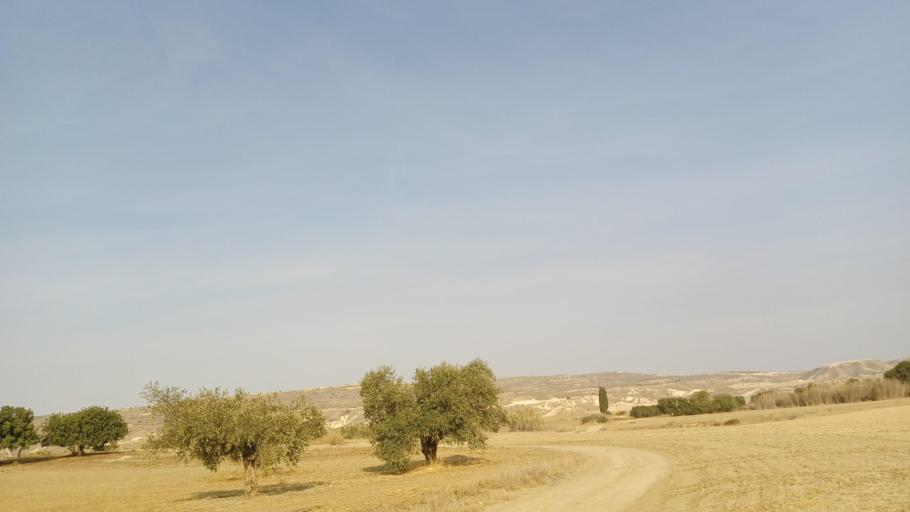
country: CY
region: Larnaka
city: Troulloi
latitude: 35.0334
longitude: 33.6062
